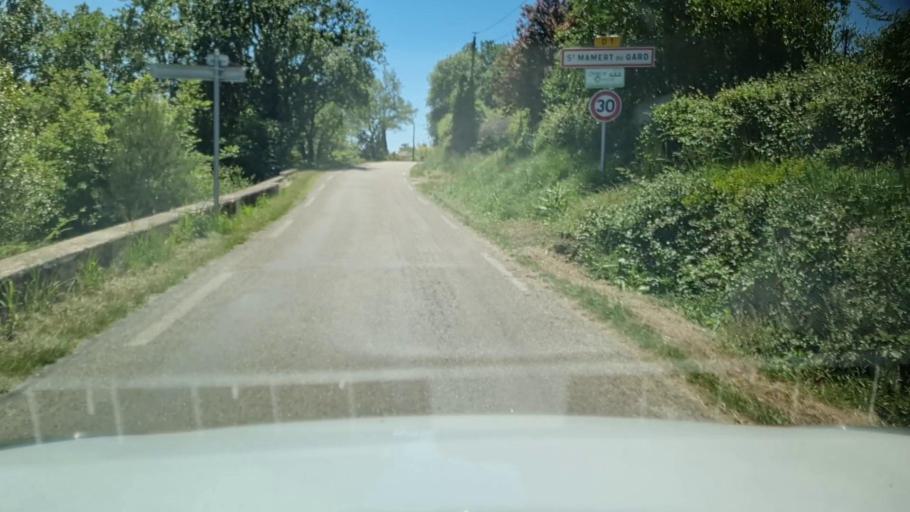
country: FR
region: Languedoc-Roussillon
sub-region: Departement du Gard
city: Saint-Mamert-du-Gard
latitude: 43.8943
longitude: 4.1884
